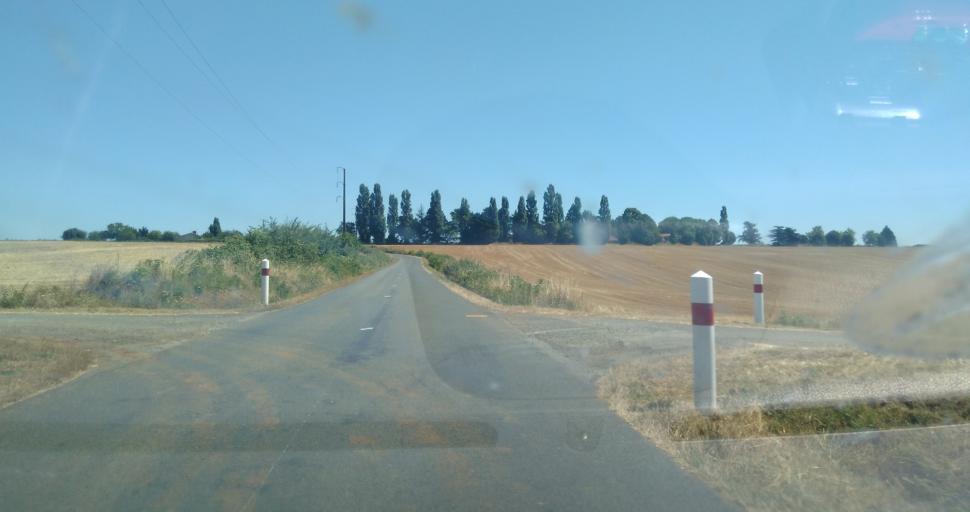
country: FR
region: Pays de la Loire
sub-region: Departement de la Vendee
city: Sainte-Hermine
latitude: 46.5774
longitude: -1.0464
